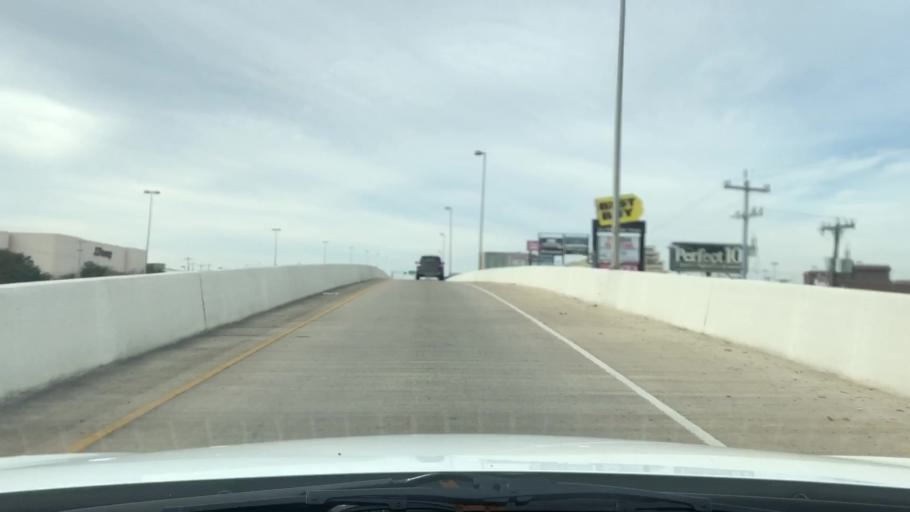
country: US
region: Texas
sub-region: Bexar County
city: Castle Hills
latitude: 29.5210
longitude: -98.4937
